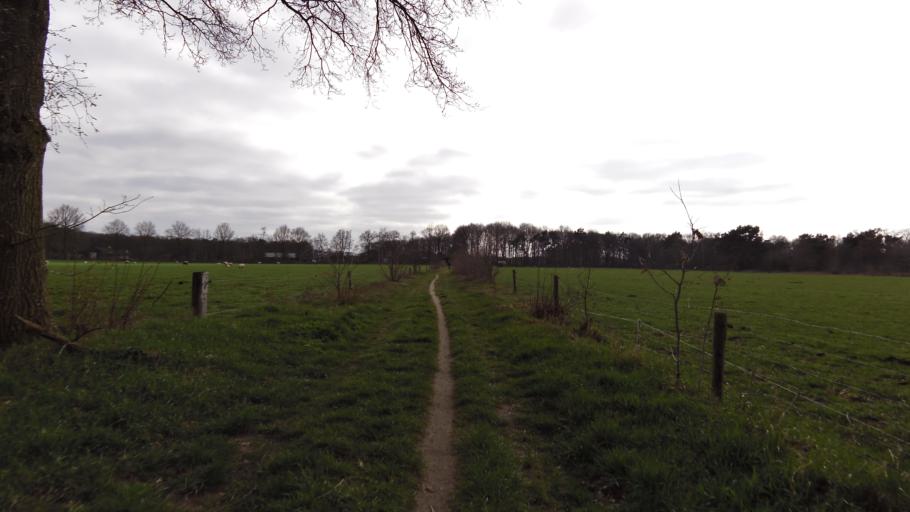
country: NL
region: Gelderland
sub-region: Gemeente Barneveld
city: Voorthuizen
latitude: 52.2026
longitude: 5.5940
